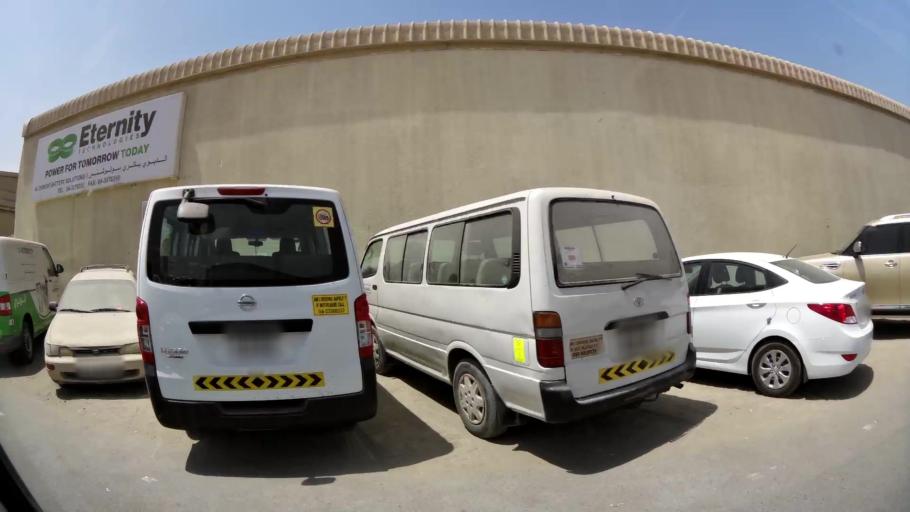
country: AE
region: Ash Shariqah
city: Sharjah
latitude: 25.2958
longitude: 55.4002
